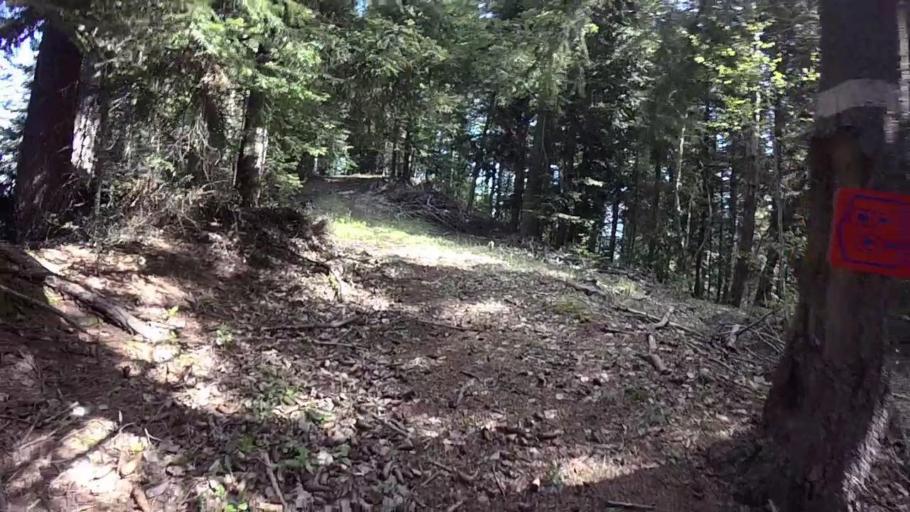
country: FR
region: Provence-Alpes-Cote d'Azur
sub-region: Departement des Alpes-de-Haute-Provence
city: Seyne-les-Alpes
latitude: 44.3311
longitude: 6.3711
